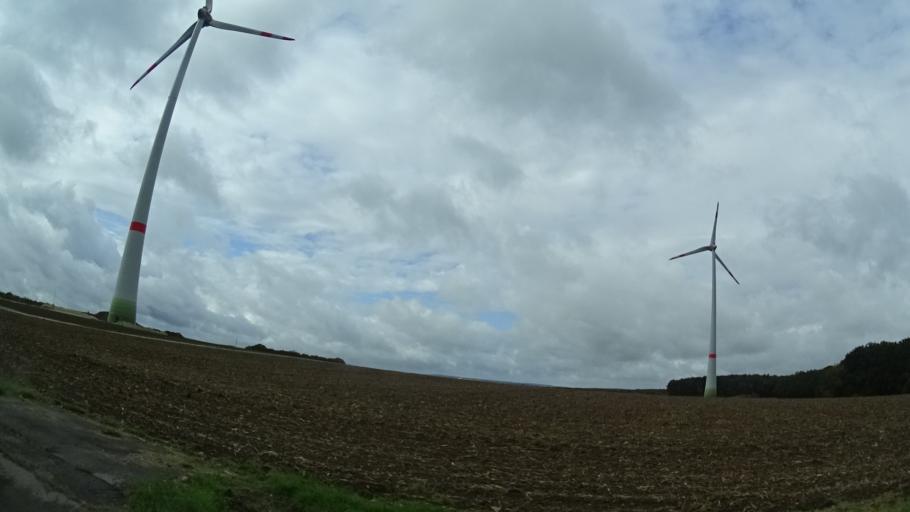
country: DE
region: Bavaria
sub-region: Upper Franconia
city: Priesendorf
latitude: 49.9102
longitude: 10.7374
